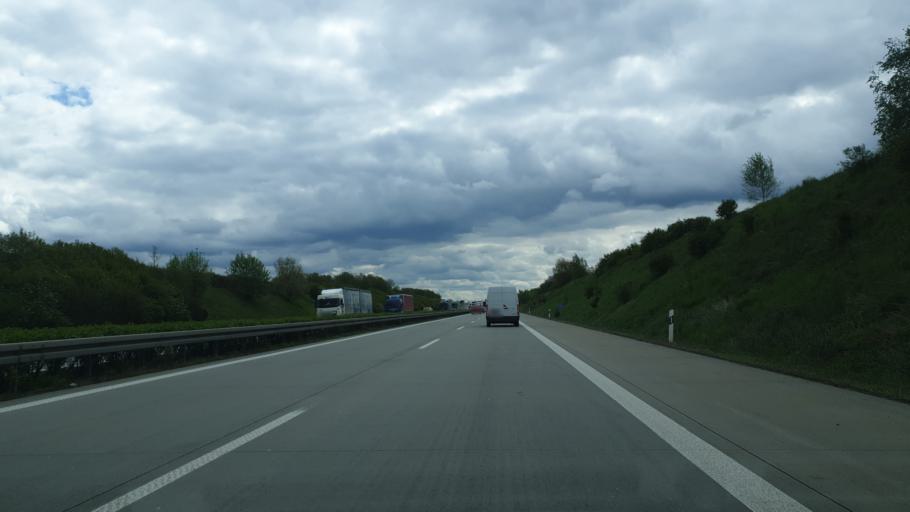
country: DE
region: Saxony
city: Niederdorf
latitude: 50.7662
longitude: 12.8116
